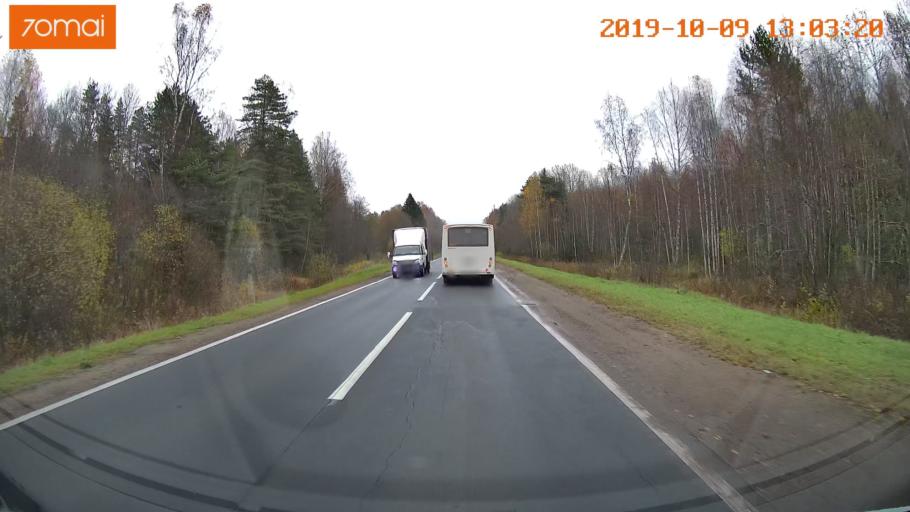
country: RU
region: Jaroslavl
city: Lyubim
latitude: 58.3595
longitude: 40.5232
